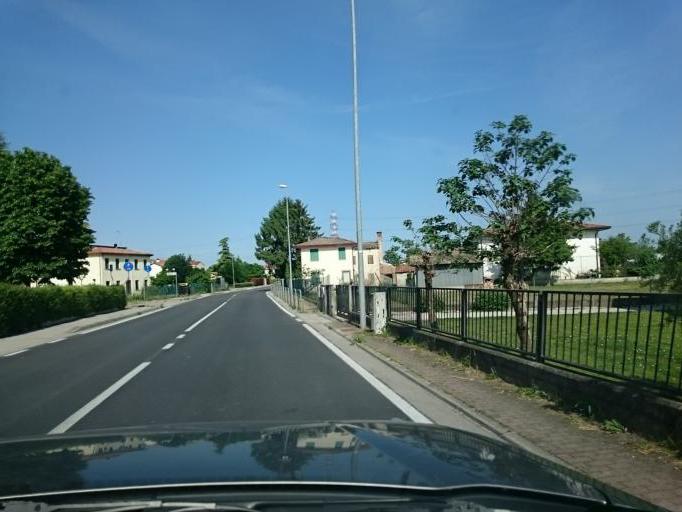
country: IT
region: Veneto
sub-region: Provincia di Venezia
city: Mira Taglio
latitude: 45.4173
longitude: 12.1299
